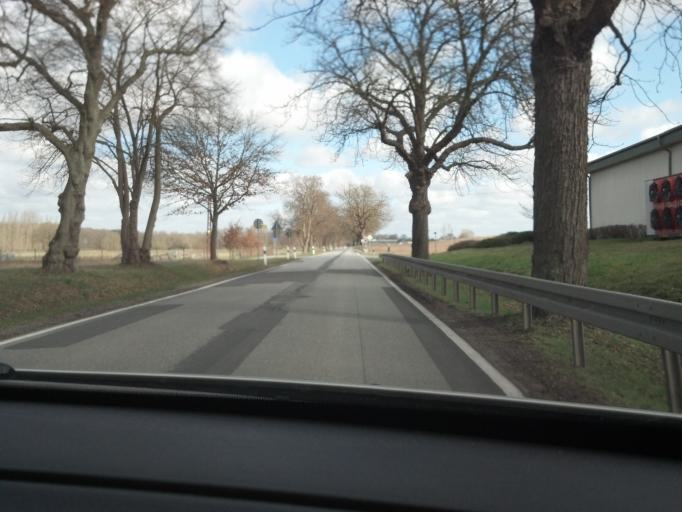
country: DE
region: Mecklenburg-Vorpommern
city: Boizenburg
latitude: 53.4151
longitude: 10.7429
